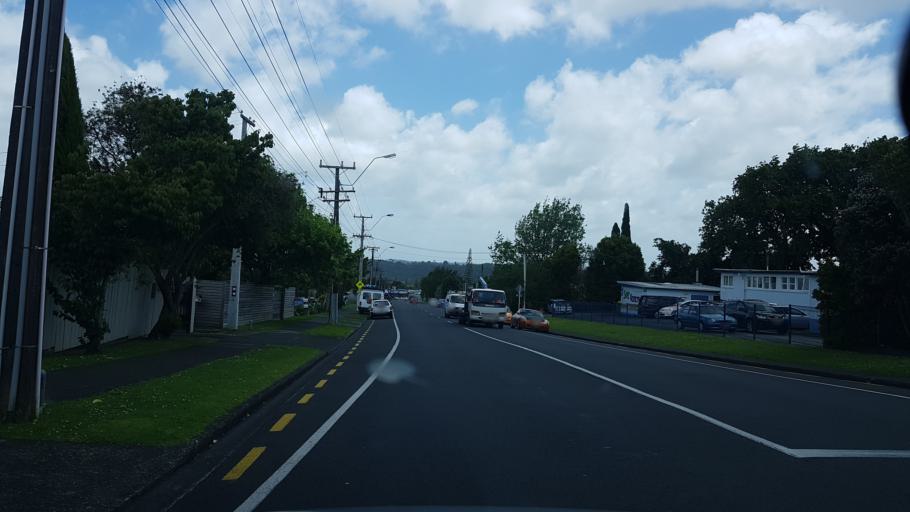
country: NZ
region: Auckland
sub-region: Auckland
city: North Shore
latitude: -36.8007
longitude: 174.7030
